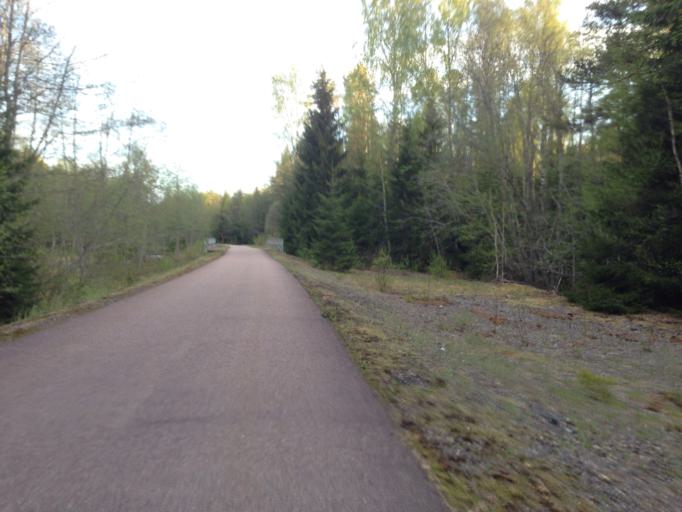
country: SE
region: Dalarna
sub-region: Ludvika Kommun
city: Grangesberg
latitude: 60.1356
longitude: 15.0729
